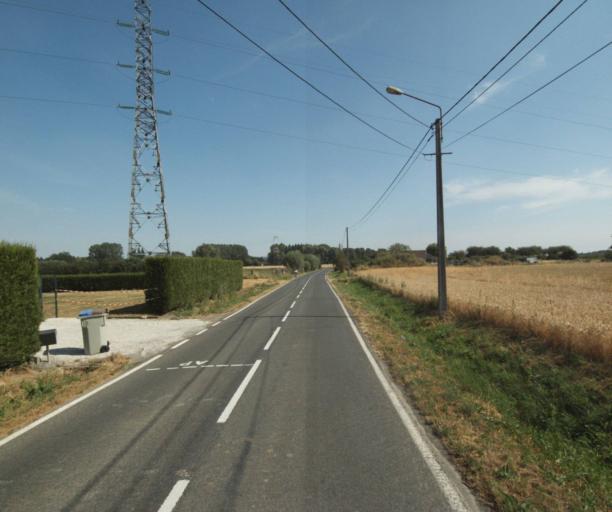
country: FR
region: Nord-Pas-de-Calais
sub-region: Departement du Nord
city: Linselles
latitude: 50.7149
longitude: 3.0643
